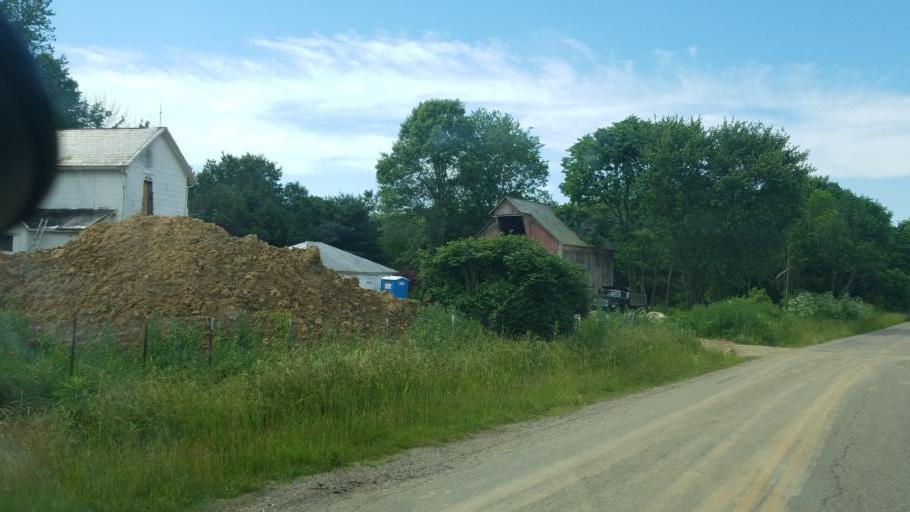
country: US
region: Ohio
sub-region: Knox County
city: Gambier
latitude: 40.2921
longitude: -82.3563
